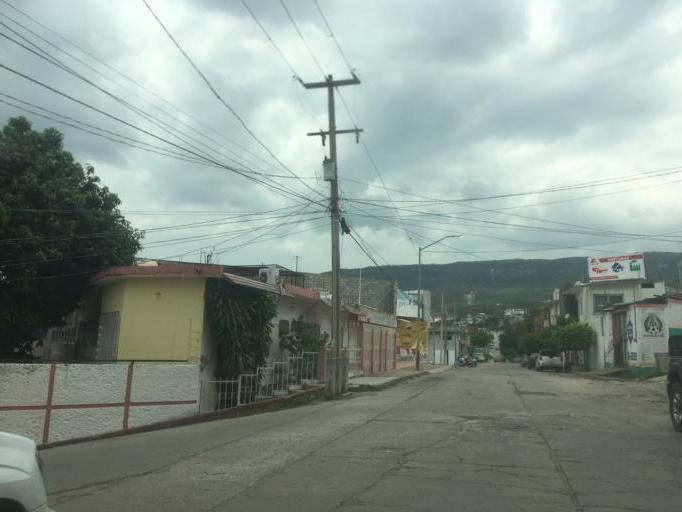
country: MX
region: Chiapas
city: Tuxtla Gutierrez
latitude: 16.7471
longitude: -93.1253
